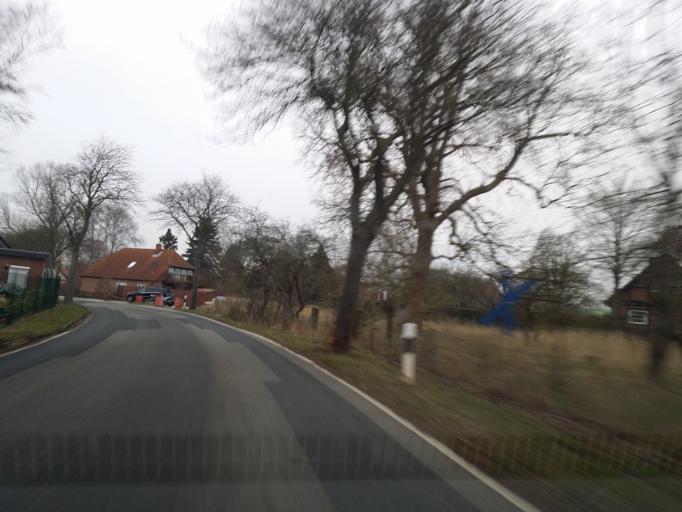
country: DE
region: Schleswig-Holstein
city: Grossenbrode
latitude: 54.4708
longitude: 11.0991
